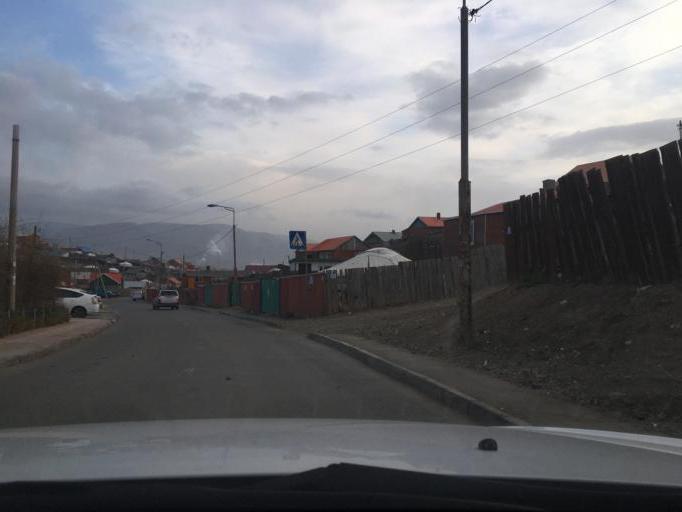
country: MN
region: Ulaanbaatar
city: Ulaanbaatar
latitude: 47.9305
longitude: 106.8582
